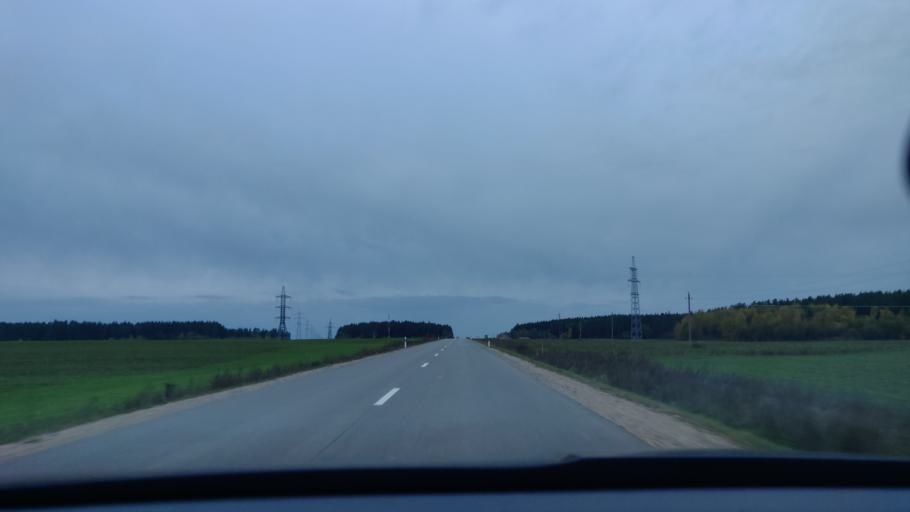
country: LT
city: Lentvaris
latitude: 54.5946
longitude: 25.0396
